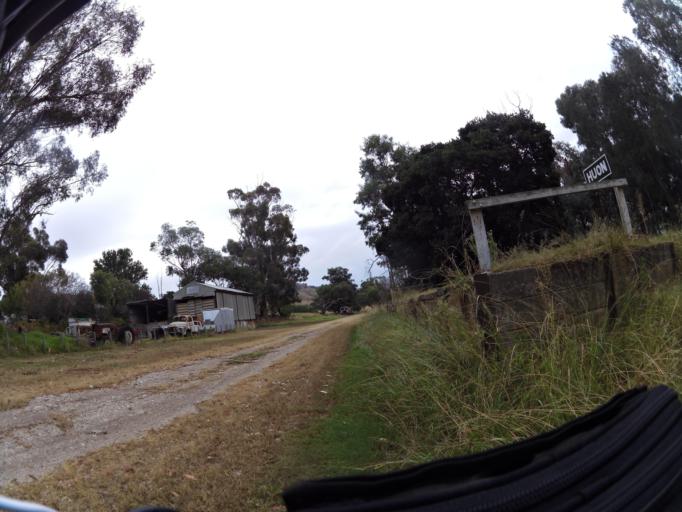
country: AU
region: New South Wales
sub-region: Albury Municipality
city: East Albury
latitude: -36.2190
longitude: 147.0657
